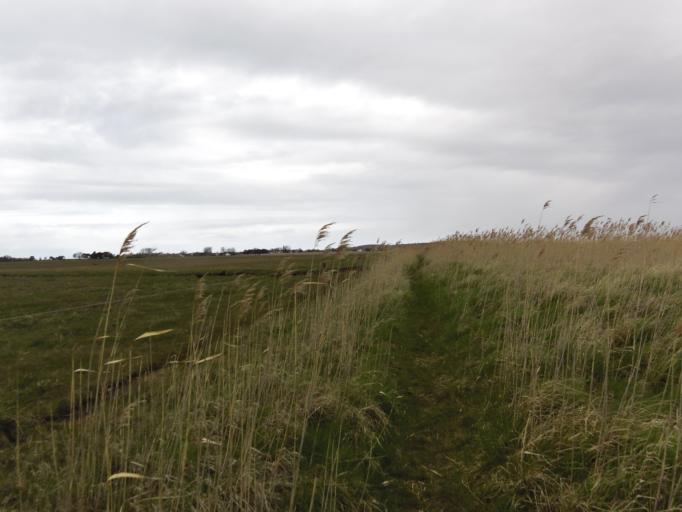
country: DE
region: Mecklenburg-Vorpommern
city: Hiddensee
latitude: 54.5514
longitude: 13.1161
